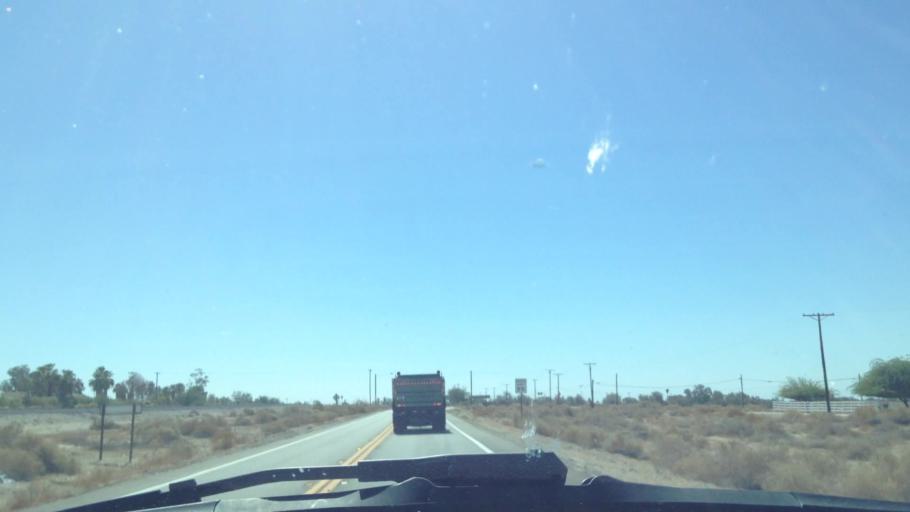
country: US
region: California
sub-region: Riverside County
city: Mecca
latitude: 33.5200
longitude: -115.9342
